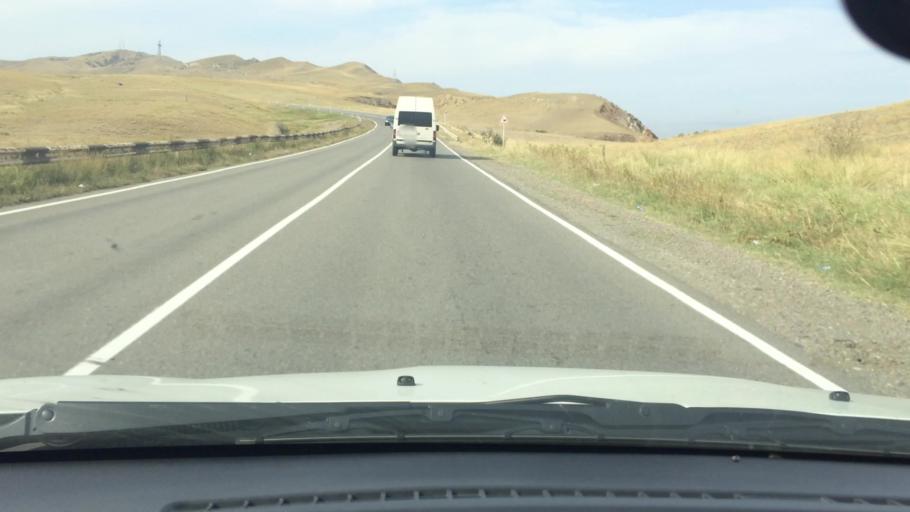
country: GE
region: Kvemo Kartli
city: Rust'avi
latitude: 41.5314
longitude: 44.9777
